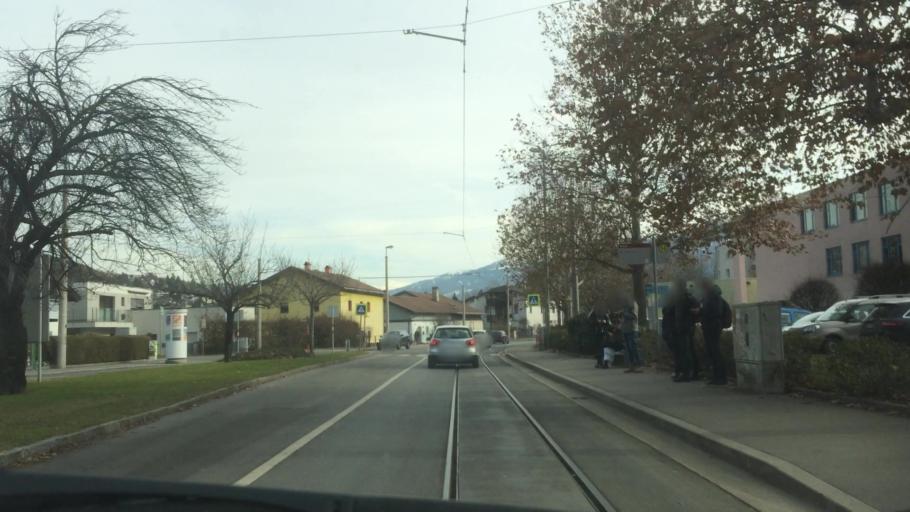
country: AT
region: Tyrol
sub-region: Politischer Bezirk Innsbruck Land
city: Vols
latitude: 47.2651
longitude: 11.3482
